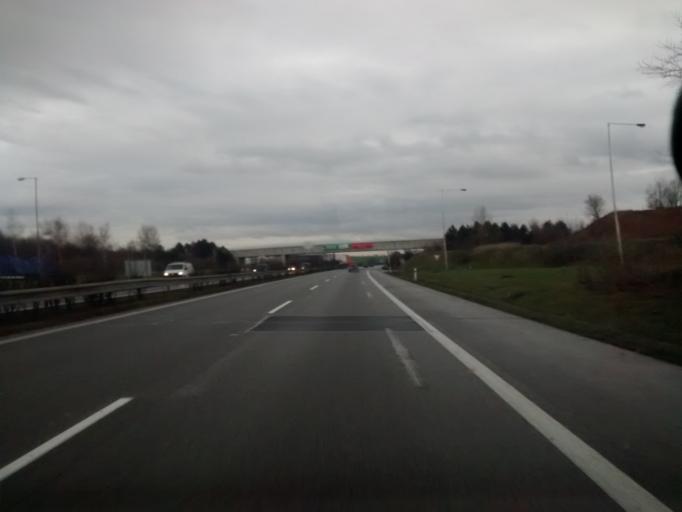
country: CZ
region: Central Bohemia
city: Odolena Voda
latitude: 50.2064
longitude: 14.4353
